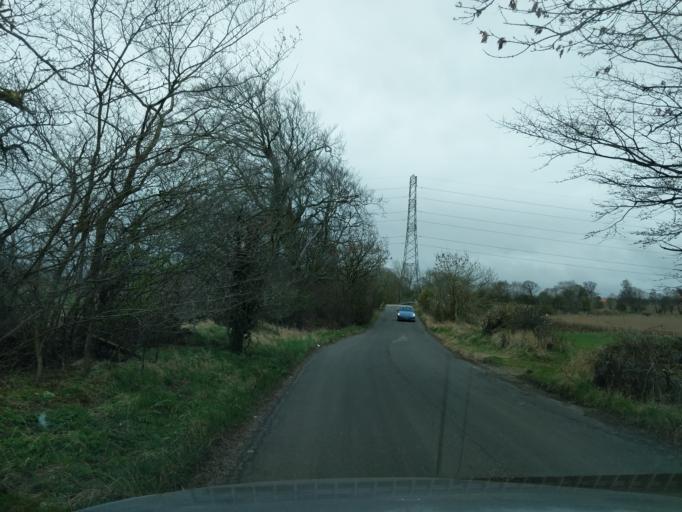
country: GB
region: Scotland
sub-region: Edinburgh
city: Balerno
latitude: 55.8951
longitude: -3.3484
